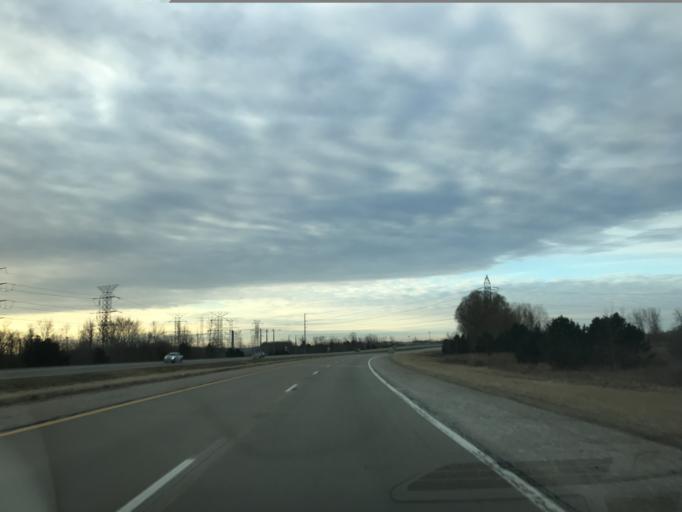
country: US
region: Michigan
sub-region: Macomb County
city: Romeo
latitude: 42.7638
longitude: -83.0092
